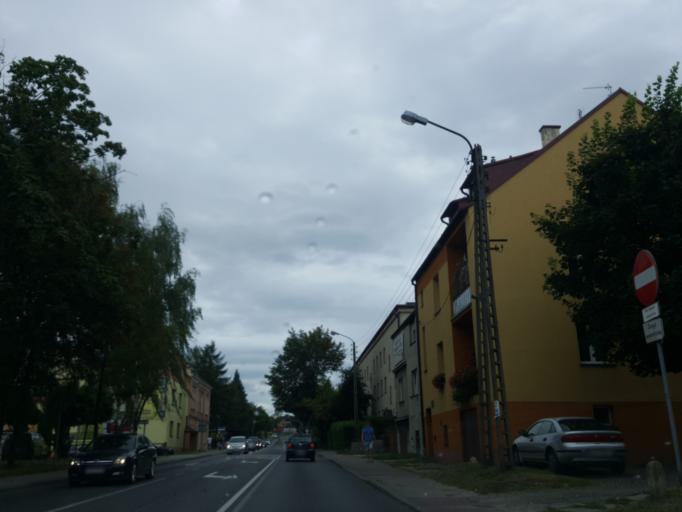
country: PL
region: Lesser Poland Voivodeship
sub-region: Powiat chrzanowski
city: Chrzanow
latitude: 50.1408
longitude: 19.3969
